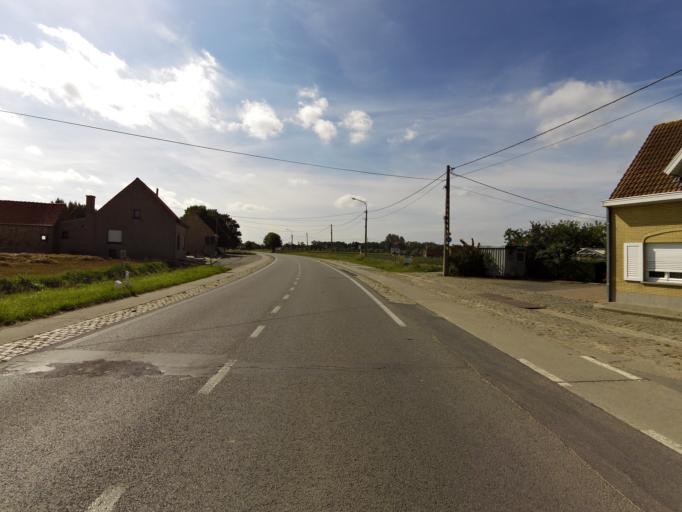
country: BE
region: Flanders
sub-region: Provincie West-Vlaanderen
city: Diksmuide
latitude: 50.9915
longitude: 2.8702
